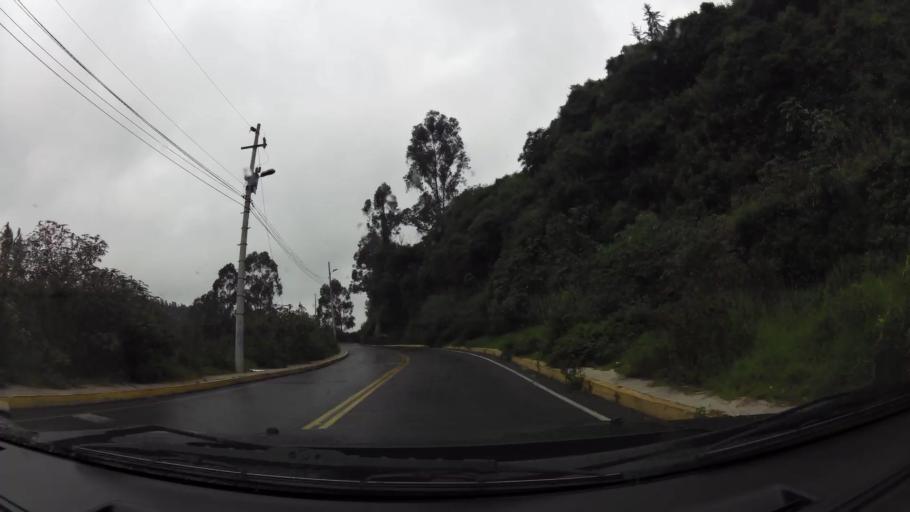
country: EC
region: Pichincha
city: Sangolqui
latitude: -0.2718
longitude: -78.4491
